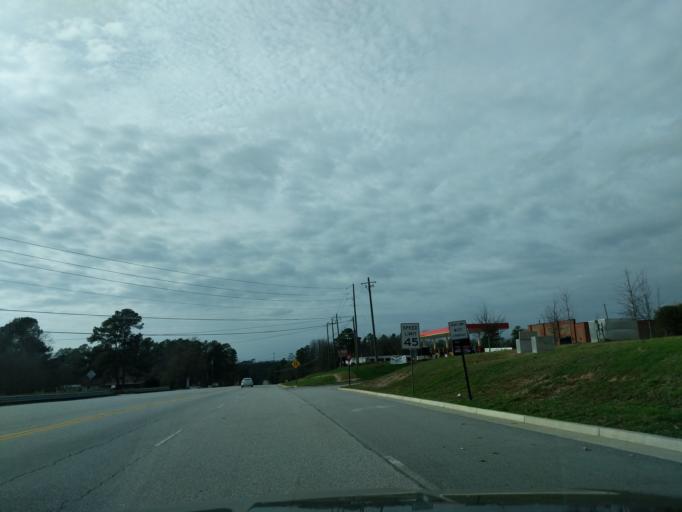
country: US
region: Georgia
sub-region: Columbia County
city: Evans
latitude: 33.4745
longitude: -82.1297
